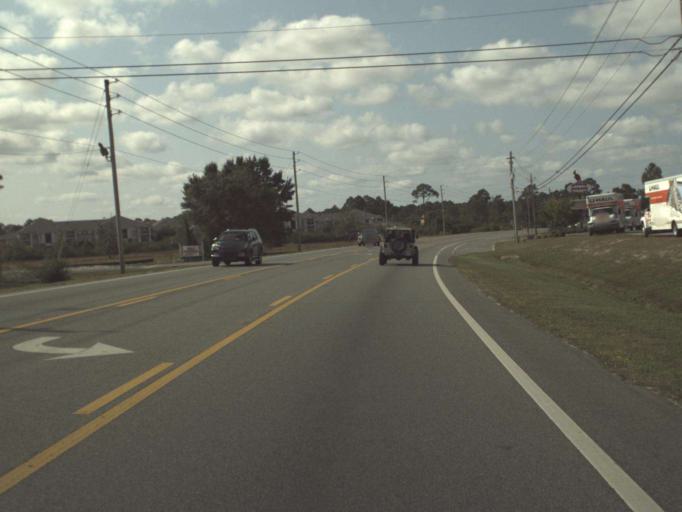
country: US
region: Florida
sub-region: Bay County
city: Lynn Haven
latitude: 30.2217
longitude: -85.6634
